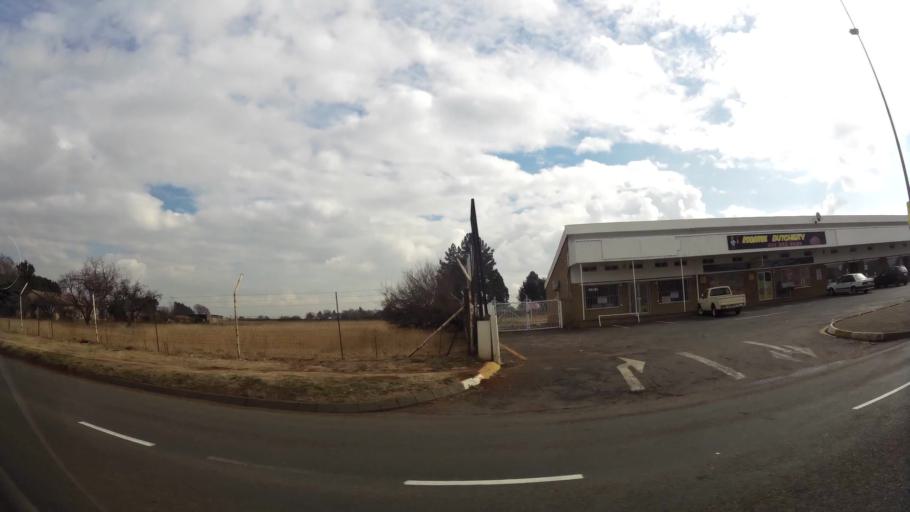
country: ZA
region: Gauteng
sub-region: Sedibeng District Municipality
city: Meyerton
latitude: -26.5886
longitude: 28.0034
